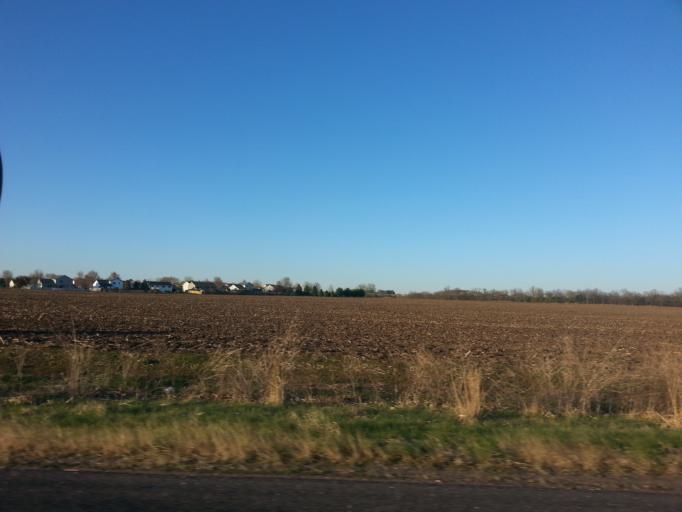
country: US
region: Minnesota
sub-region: Dakota County
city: Hastings
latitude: 44.7033
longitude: -92.8307
